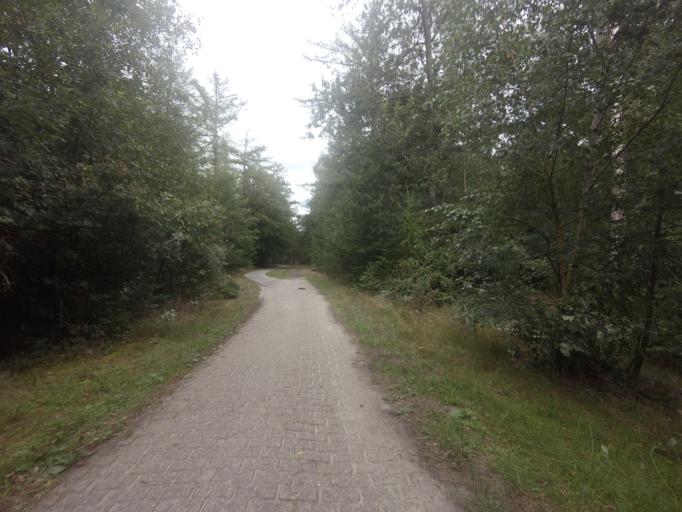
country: NL
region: Drenthe
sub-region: Gemeente Westerveld
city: Dwingeloo
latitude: 52.8964
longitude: 6.2949
